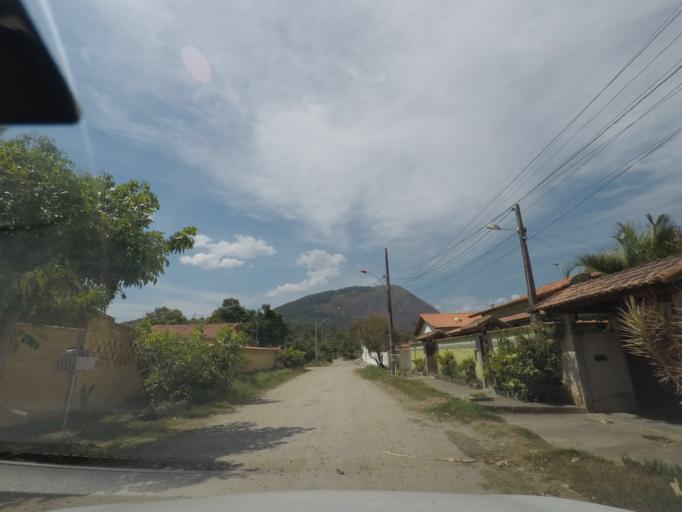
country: BR
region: Rio de Janeiro
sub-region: Marica
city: Marica
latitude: -22.9549
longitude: -42.9644
